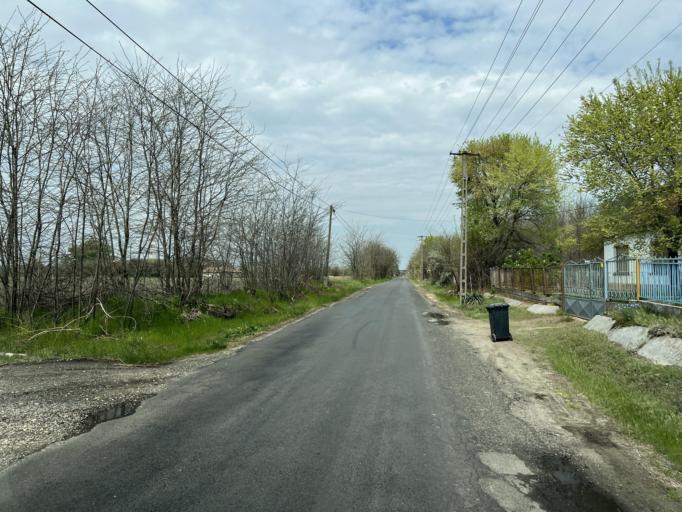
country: HU
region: Pest
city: Taborfalva
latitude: 47.1288
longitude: 19.4725
